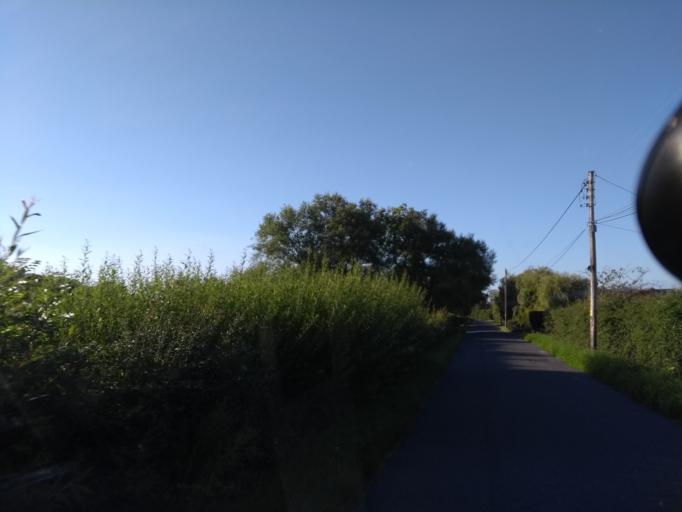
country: GB
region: England
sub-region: Somerset
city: Axbridge
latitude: 51.2692
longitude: -2.8714
